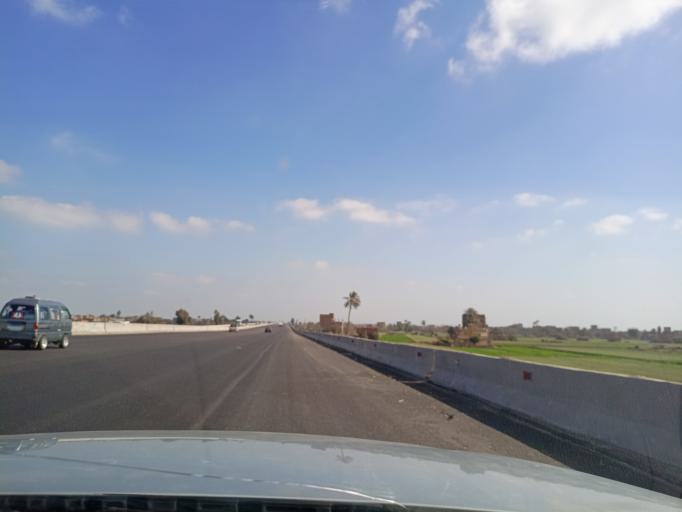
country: EG
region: Muhafazat al Minufiyah
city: Al Bajur
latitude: 30.4090
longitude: 31.0519
